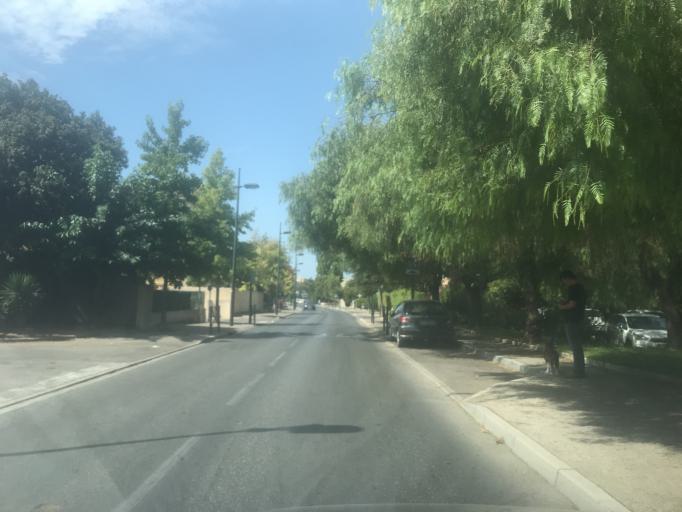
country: FR
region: Provence-Alpes-Cote d'Azur
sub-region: Departement du Var
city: Six-Fours-les-Plages
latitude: 43.0908
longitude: 5.8485
